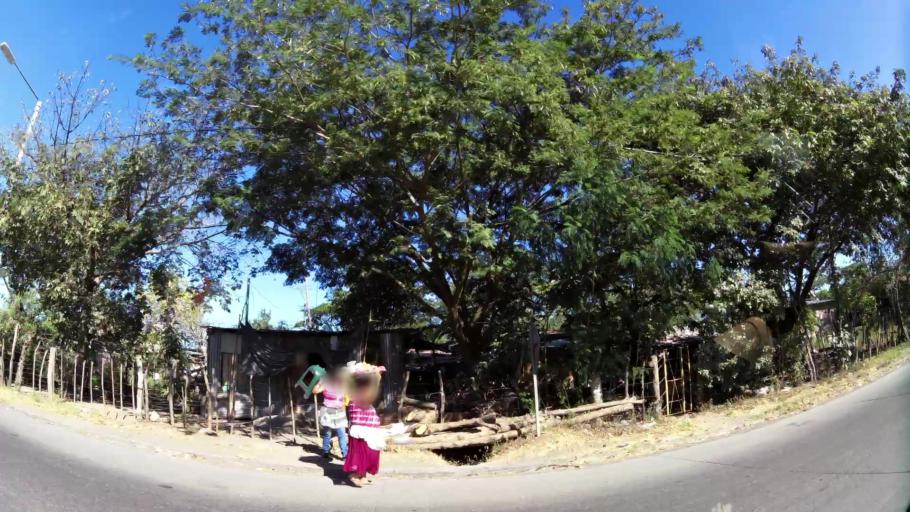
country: SV
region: San Miguel
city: San Miguel
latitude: 13.4607
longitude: -88.1507
